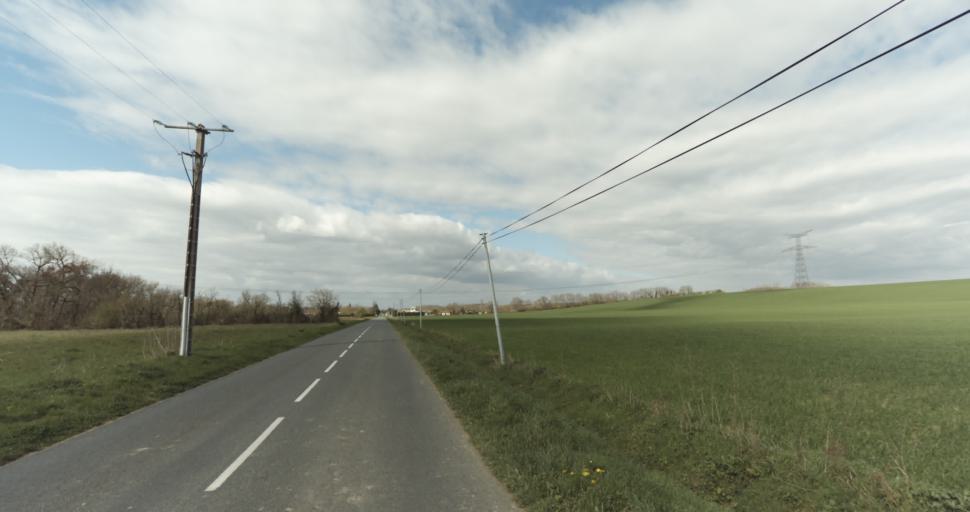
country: FR
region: Midi-Pyrenees
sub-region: Departement de la Haute-Garonne
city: Auterive
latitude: 43.3840
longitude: 1.4597
